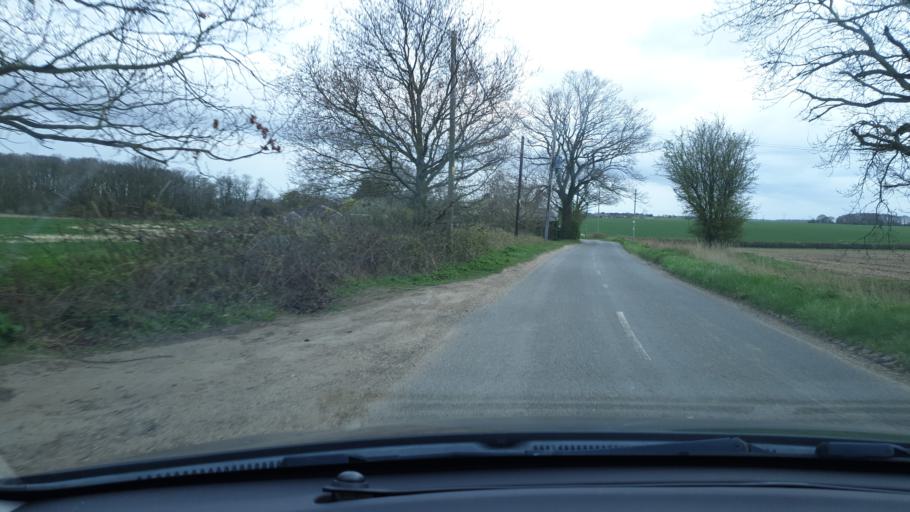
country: GB
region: England
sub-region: Essex
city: Mistley
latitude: 51.9367
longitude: 1.1749
